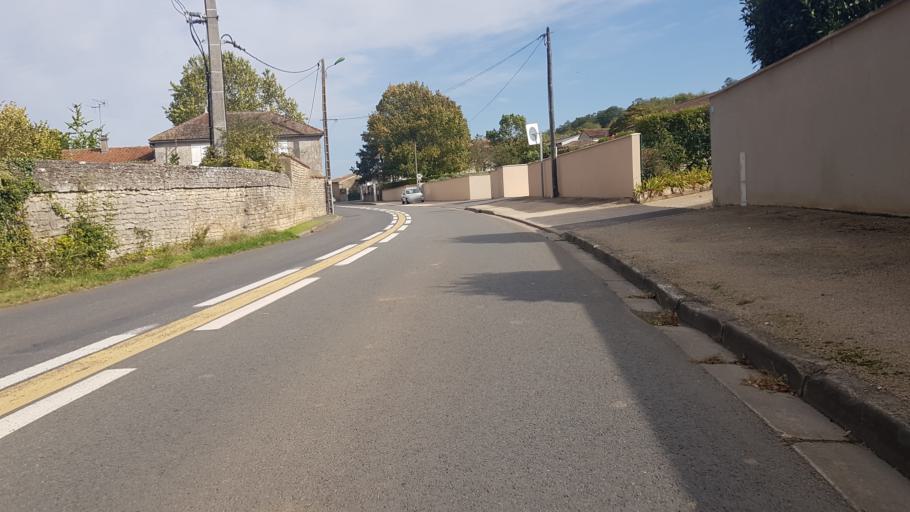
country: FR
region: Poitou-Charentes
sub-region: Departement de la Vienne
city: Chasseneuil-du-Poitou
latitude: 46.6295
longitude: 0.3685
